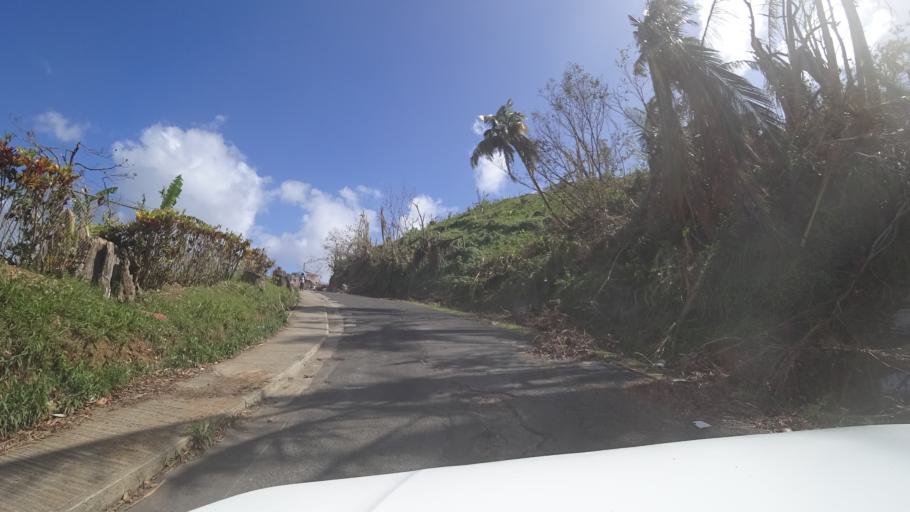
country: DM
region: Saint Patrick
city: Berekua
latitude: 15.2464
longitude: -61.3158
